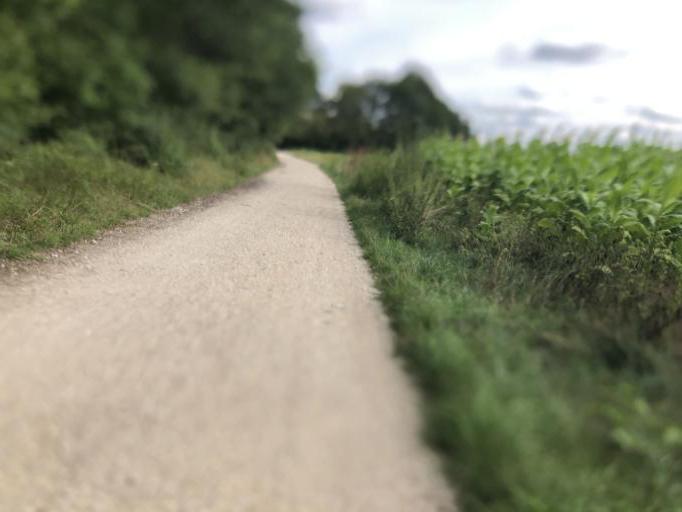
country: DE
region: Bavaria
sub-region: Regierungsbezirk Mittelfranken
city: Furth
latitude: 49.5295
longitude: 11.0023
